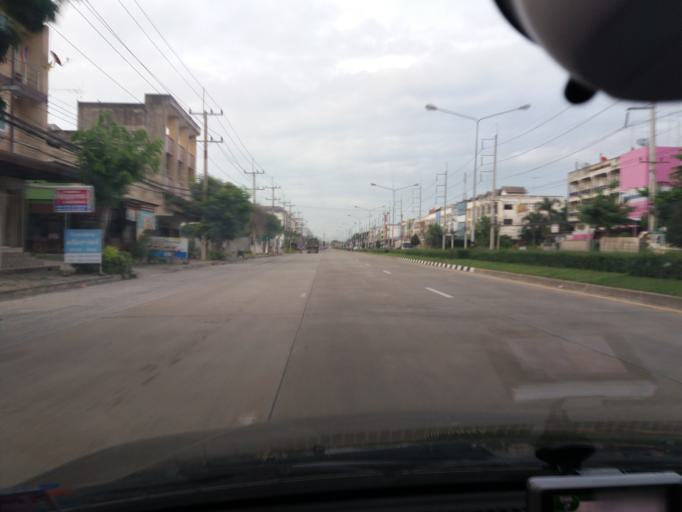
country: TH
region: Suphan Buri
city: U Thong
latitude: 14.3827
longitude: 99.8946
